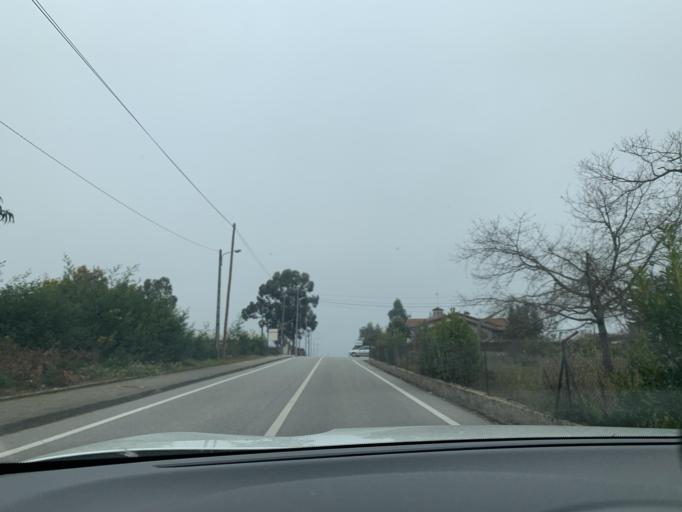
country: PT
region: Viseu
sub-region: Concelho de Tondela
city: Tondela
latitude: 40.5027
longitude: -8.0785
